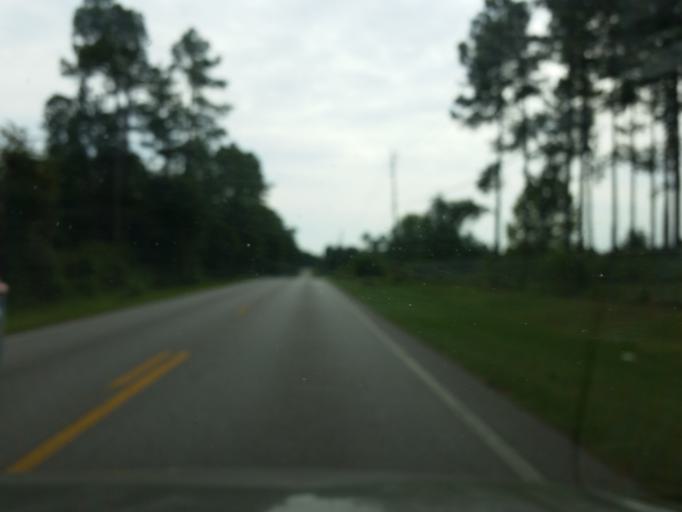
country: US
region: Florida
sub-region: Escambia County
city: Molino
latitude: 30.6728
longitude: -87.3197
